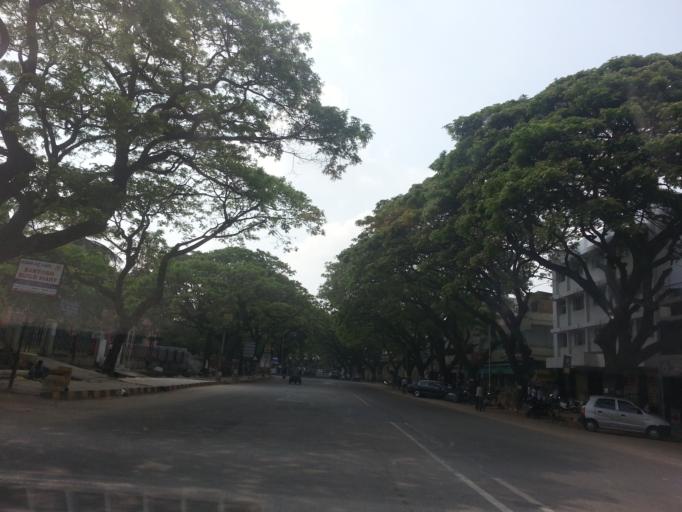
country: IN
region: Karnataka
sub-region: Mysore
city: Mysore
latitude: 12.3251
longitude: 76.6450
